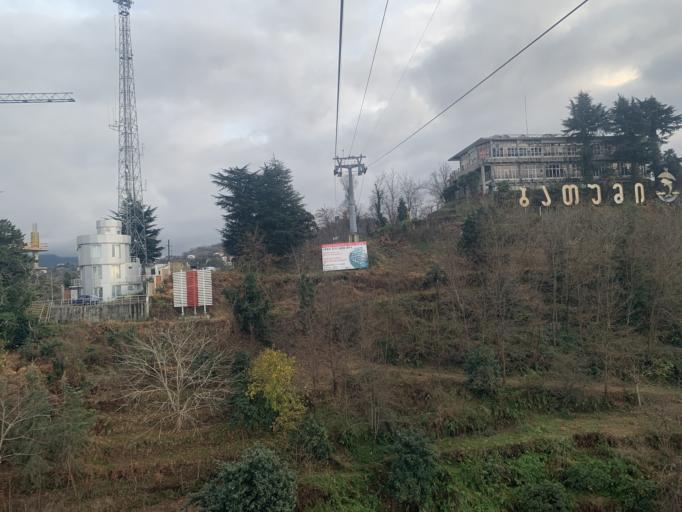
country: GE
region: Ajaria
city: Batumi
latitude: 41.6374
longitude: 41.6506
